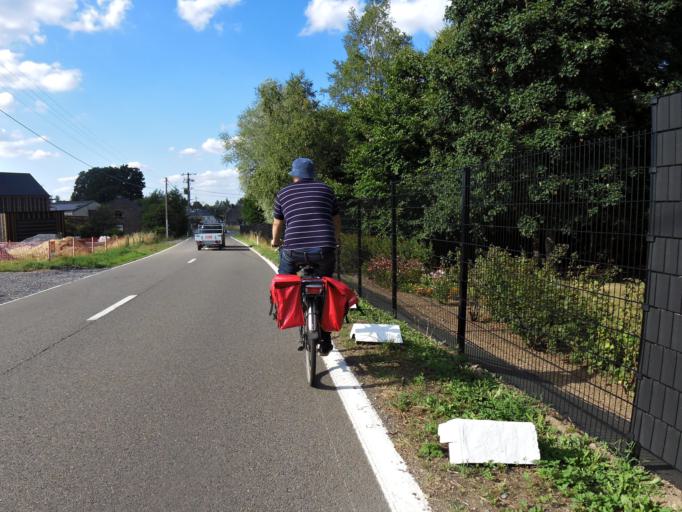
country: BE
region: Wallonia
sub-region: Province de Namur
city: Bievre
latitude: 49.9301
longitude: 5.0427
